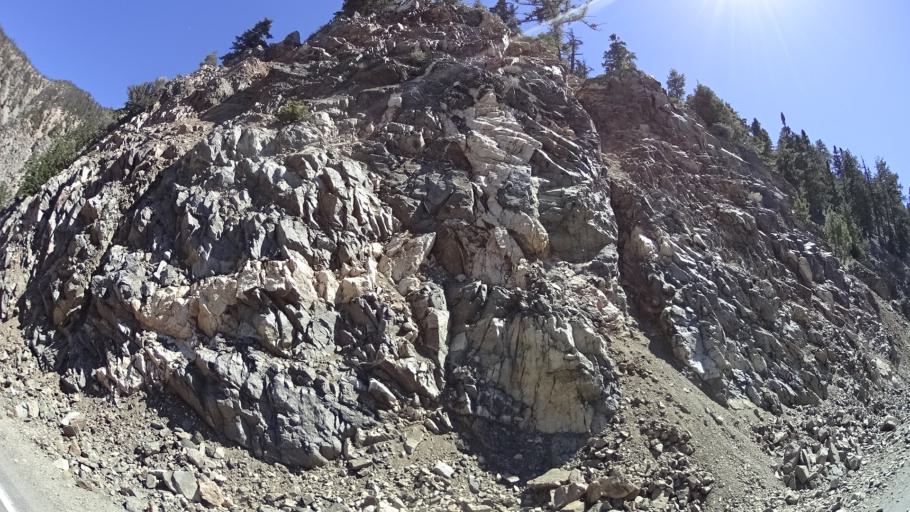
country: US
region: California
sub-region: San Bernardino County
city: Wrightwood
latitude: 34.3681
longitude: -117.7849
